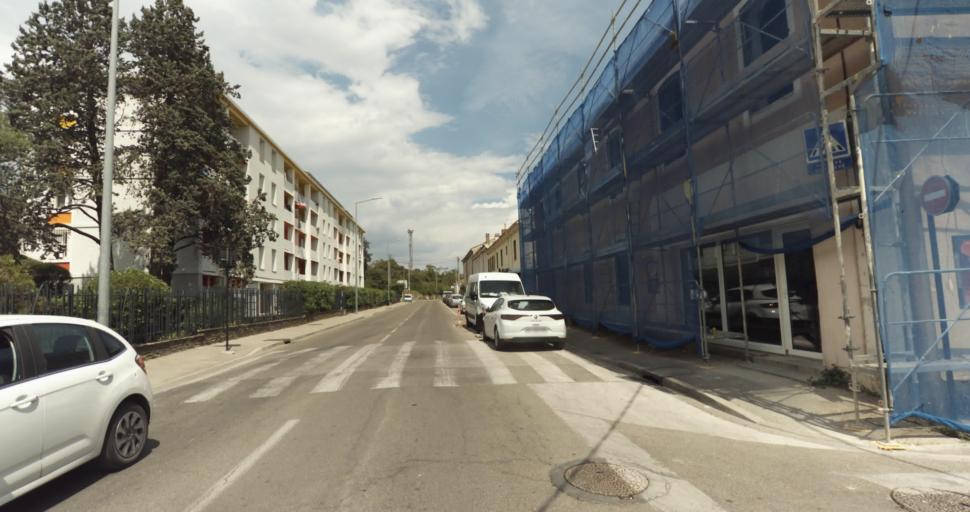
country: FR
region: Languedoc-Roussillon
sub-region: Departement du Gard
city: Nimes
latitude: 43.8451
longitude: 4.3840
